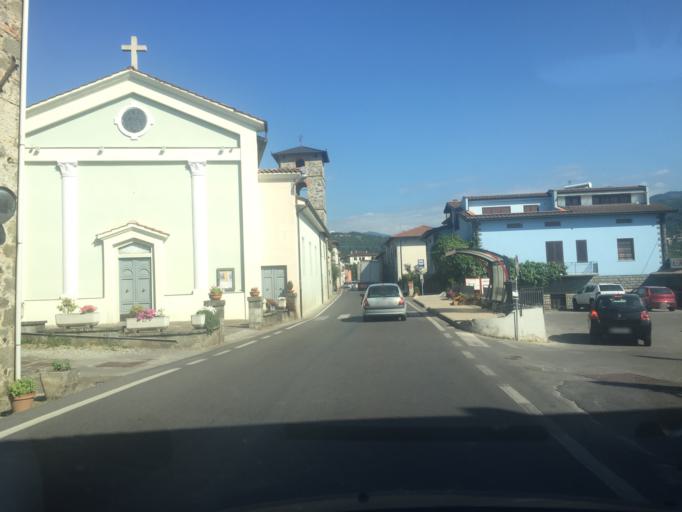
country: IT
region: Tuscany
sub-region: Provincia di Lucca
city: Villa Collemandina
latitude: 44.1345
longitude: 10.3707
